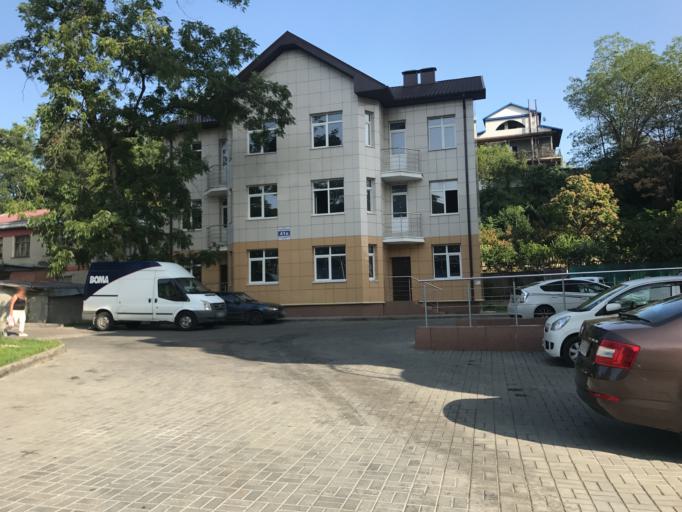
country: RU
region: Krasnodarskiy
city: Adler
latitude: 43.4205
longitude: 39.9378
